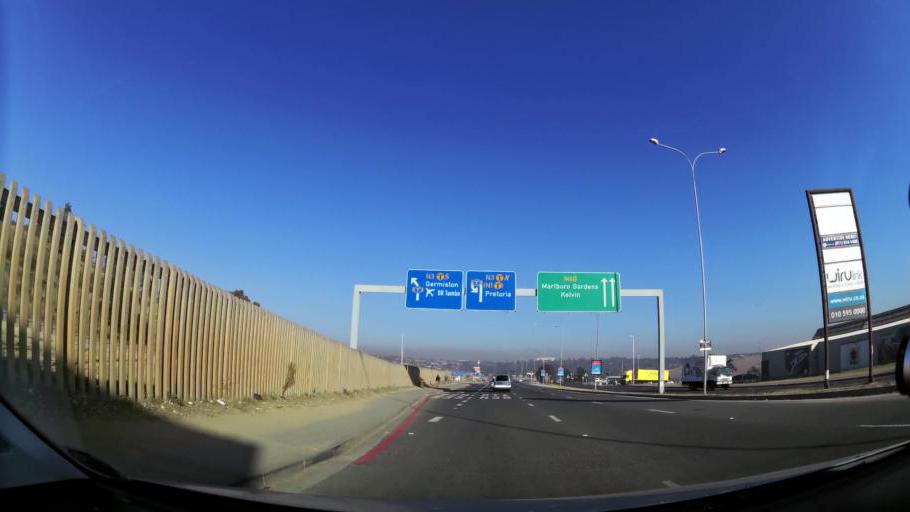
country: ZA
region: Gauteng
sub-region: City of Johannesburg Metropolitan Municipality
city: Modderfontein
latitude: -26.0821
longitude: 28.1171
